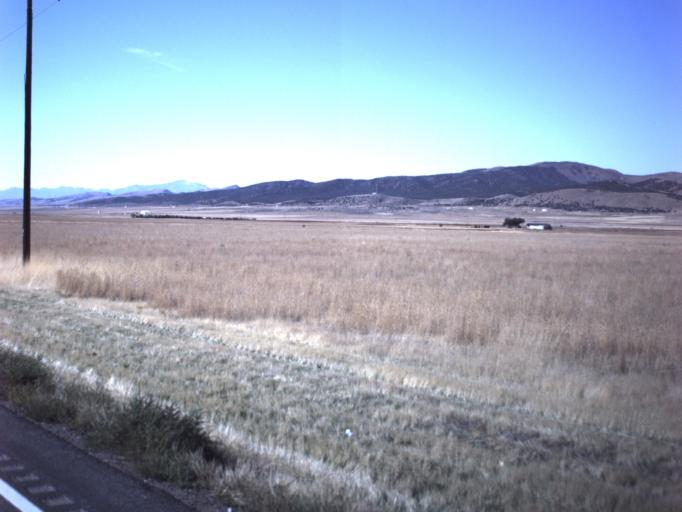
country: US
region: Utah
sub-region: Juab County
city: Nephi
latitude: 39.6486
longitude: -111.8598
